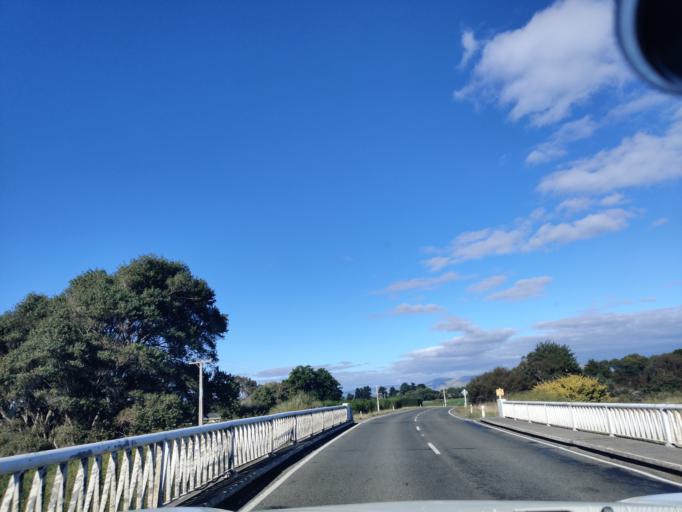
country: NZ
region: Manawatu-Wanganui
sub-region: Horowhenua District
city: Foxton
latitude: -40.4225
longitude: 175.4462
